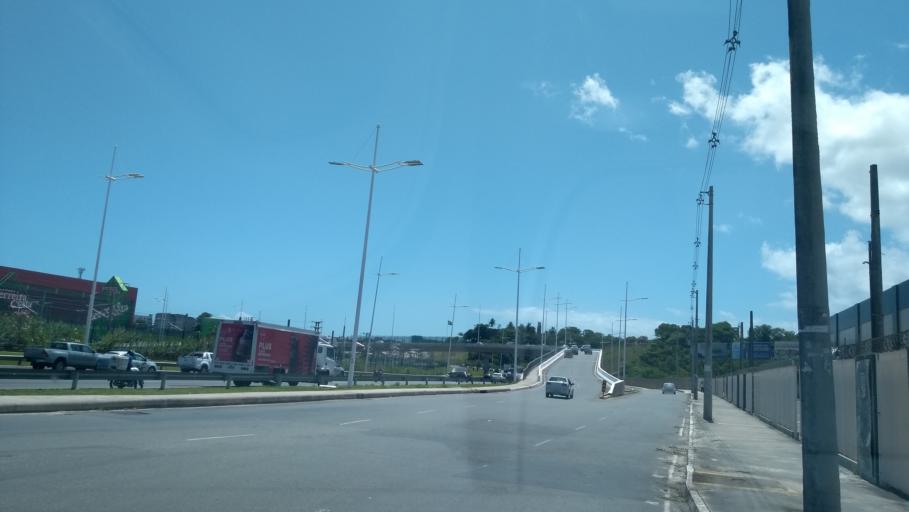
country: BR
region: Bahia
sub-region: Lauro De Freitas
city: Lauro de Freitas
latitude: -12.9387
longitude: -38.4144
